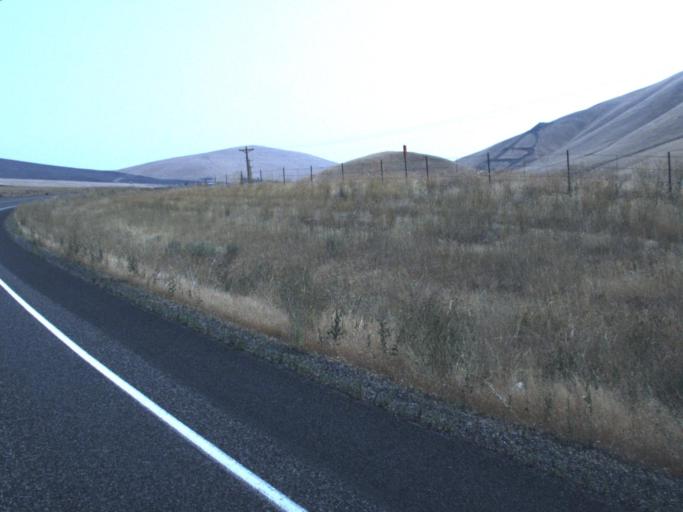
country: US
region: Washington
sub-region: Grant County
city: Desert Aire
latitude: 46.5362
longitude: -119.9117
